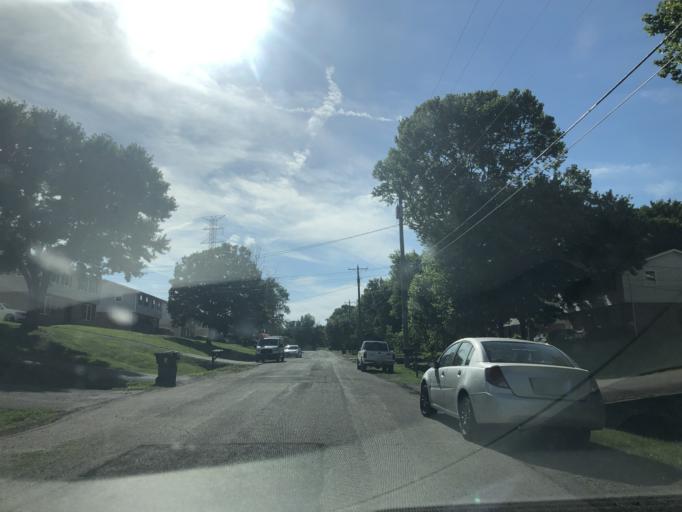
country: US
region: Tennessee
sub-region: Davidson County
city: Belle Meade
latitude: 36.0620
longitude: -86.9344
